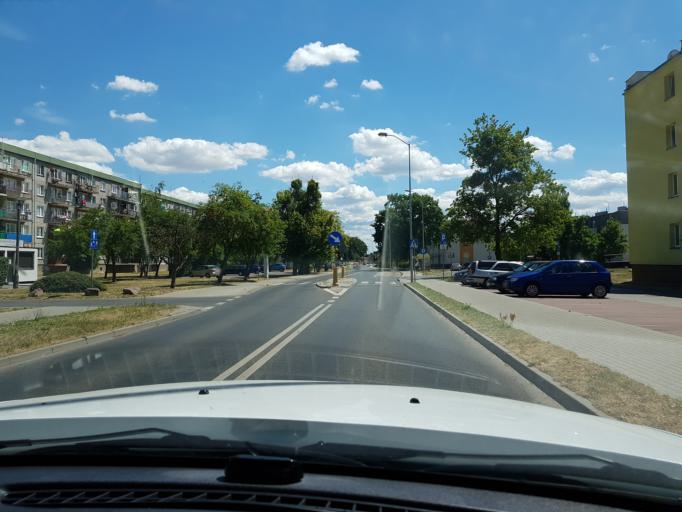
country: PL
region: West Pomeranian Voivodeship
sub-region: Powiat mysliborski
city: Mysliborz
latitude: 52.9245
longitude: 14.8746
